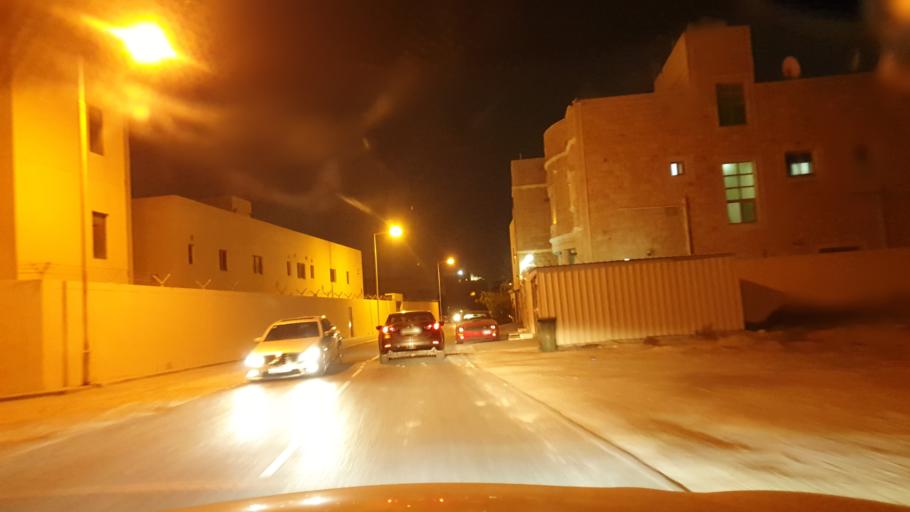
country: BH
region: Manama
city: Jidd Hafs
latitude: 26.1965
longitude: 50.4884
